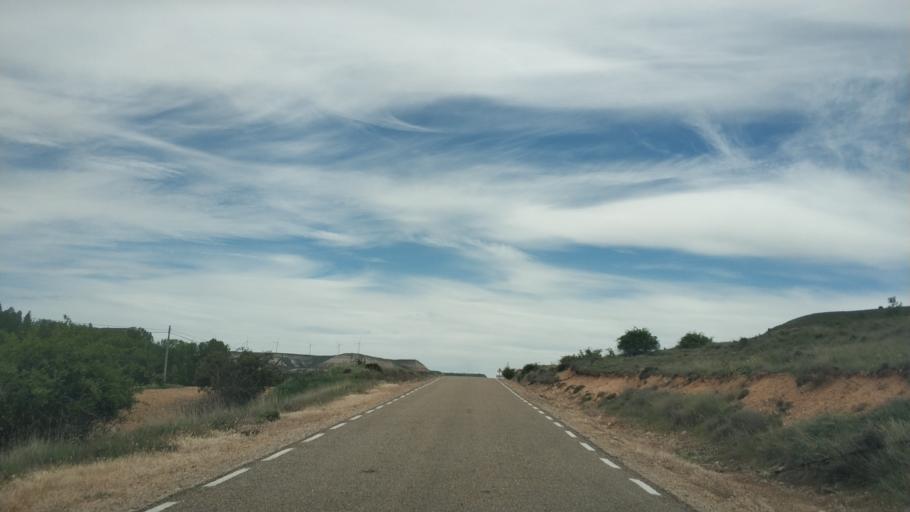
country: ES
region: Castille and Leon
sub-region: Provincia de Soria
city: Caltojar
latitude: 41.4247
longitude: -2.7869
